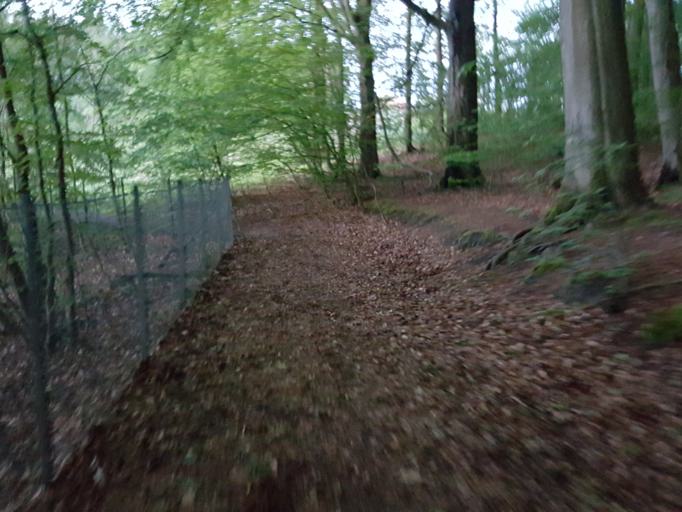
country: DK
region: Capital Region
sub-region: Rudersdal Kommune
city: Birkerod
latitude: 55.8471
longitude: 12.4566
